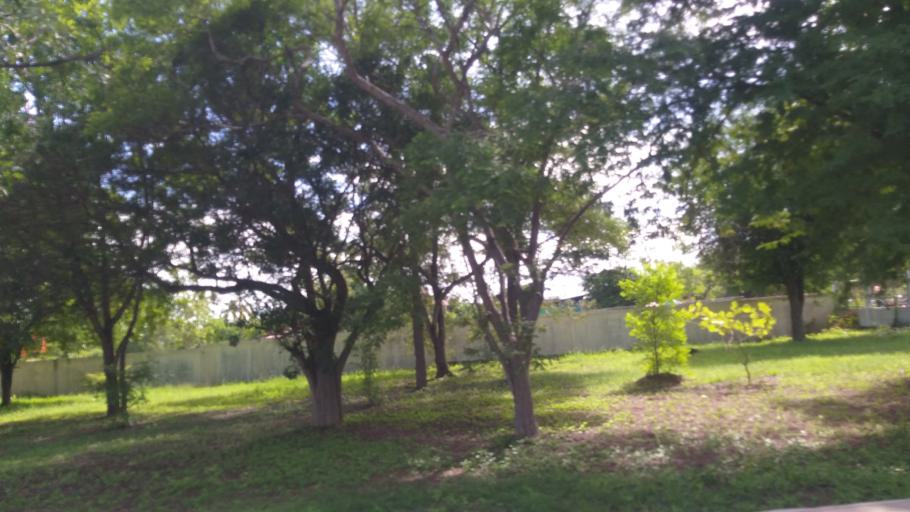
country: TH
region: Chaiyaphum
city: Ban Thaen
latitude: 16.4059
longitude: 102.3444
